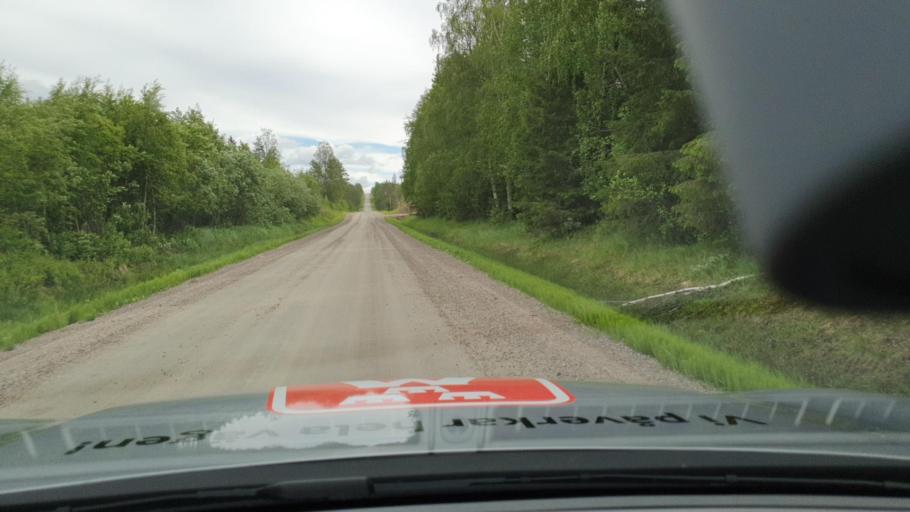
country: SE
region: Norrbotten
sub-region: Kalix Kommun
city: Kalix
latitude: 65.9231
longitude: 23.4780
